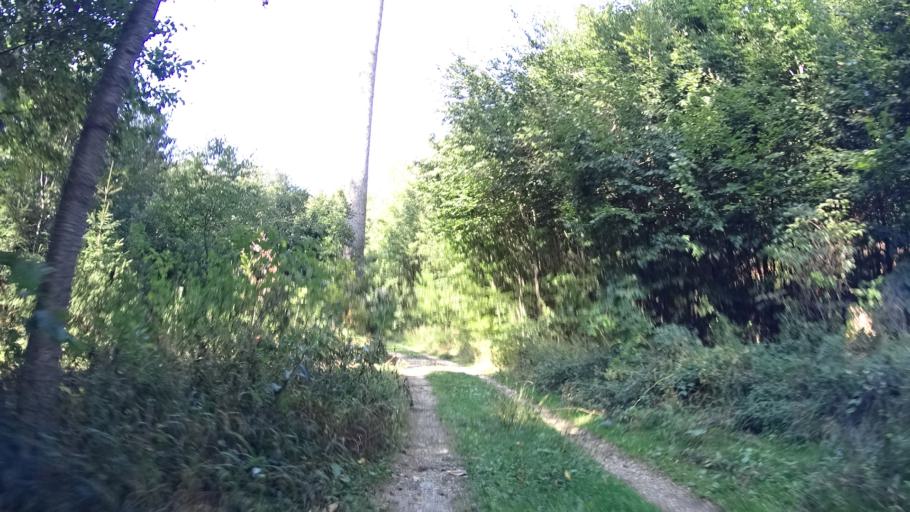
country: DE
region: Bavaria
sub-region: Upper Bavaria
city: Walting
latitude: 48.9523
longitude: 11.3554
